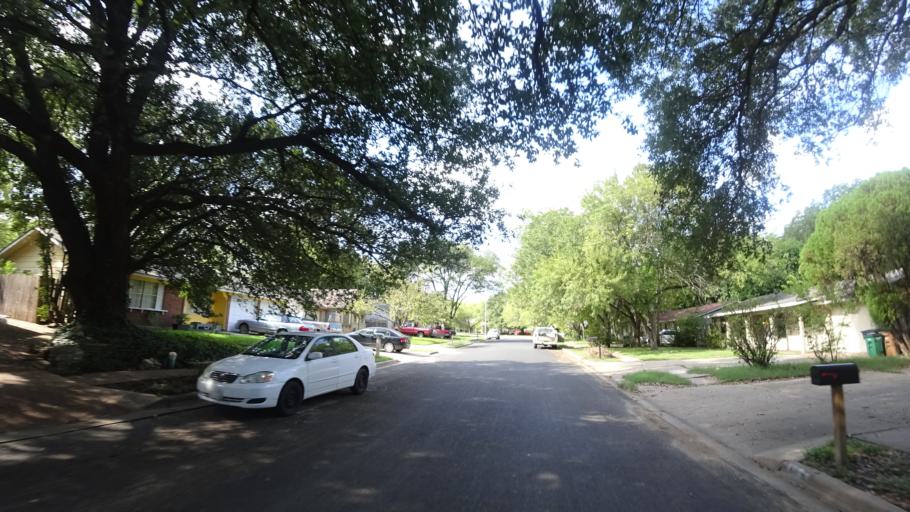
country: US
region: Texas
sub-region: Travis County
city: Onion Creek
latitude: 30.2042
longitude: -97.7858
